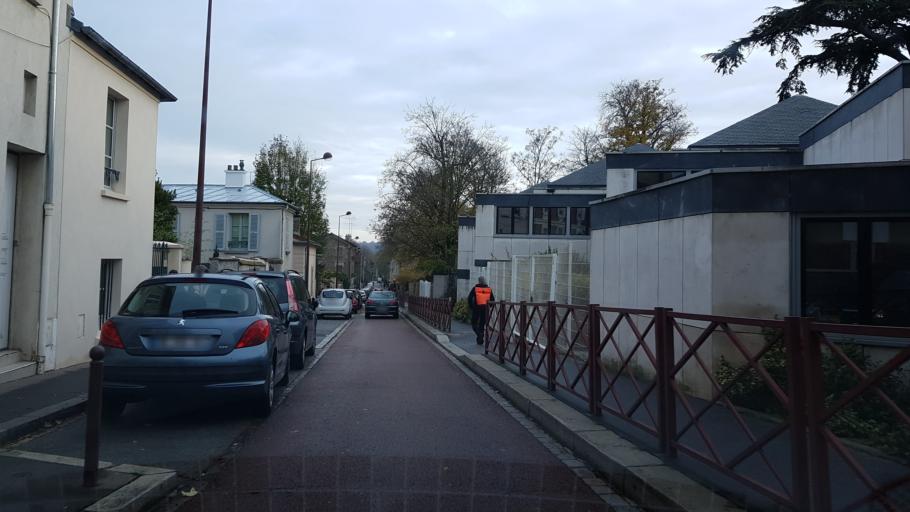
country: FR
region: Ile-de-France
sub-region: Departement des Yvelines
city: Versailles
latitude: 48.8024
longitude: 2.1460
